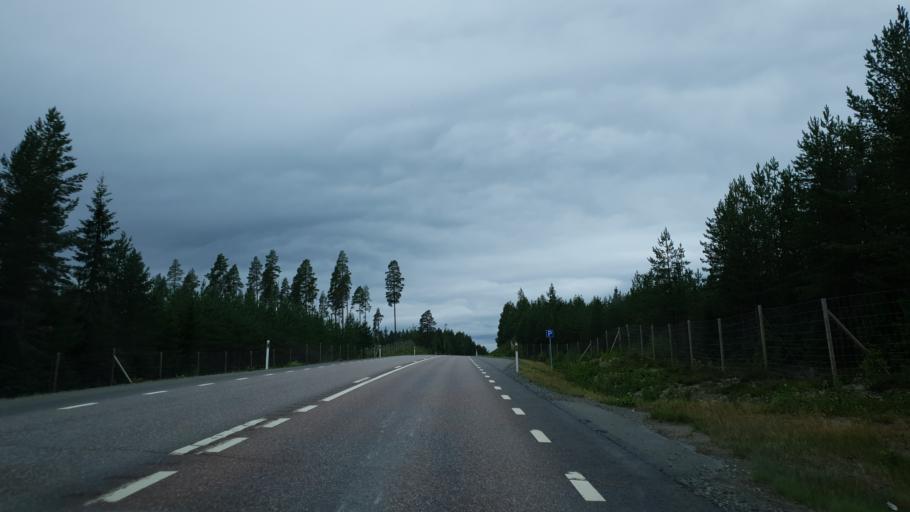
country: SE
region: Vaesterbotten
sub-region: Skelleftea Kommun
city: Viken
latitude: 64.7929
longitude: 20.7539
